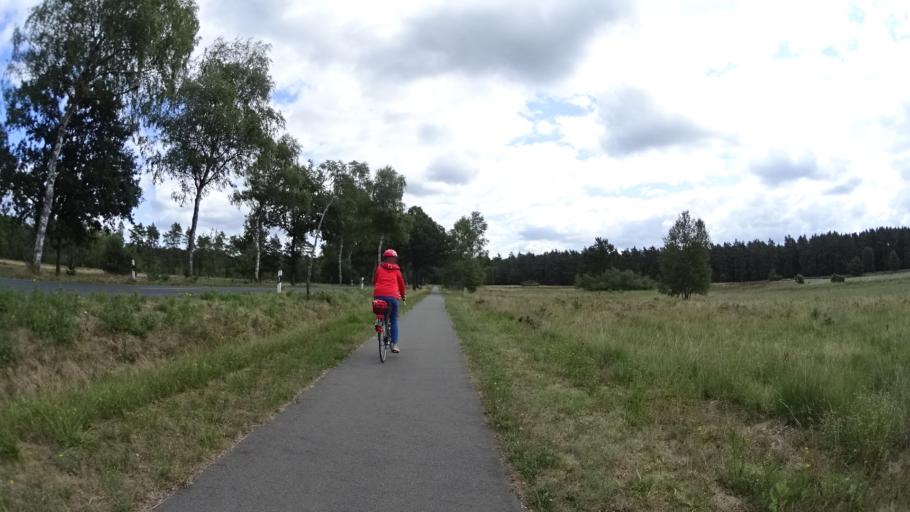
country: DE
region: Lower Saxony
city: Handeloh
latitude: 53.2374
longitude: 9.8801
